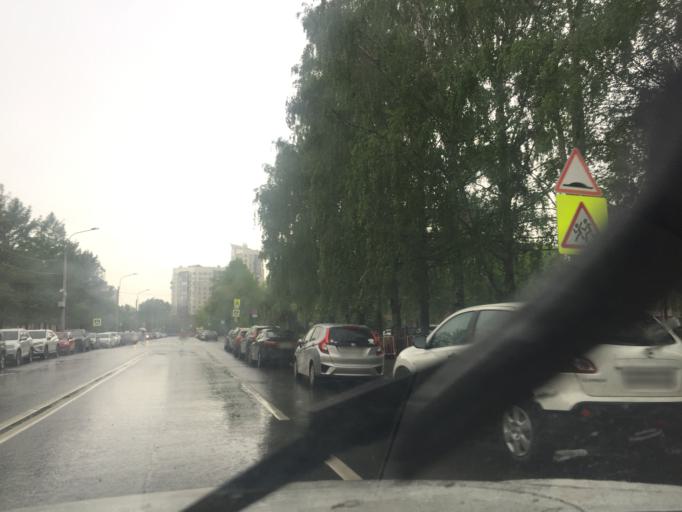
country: RU
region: St.-Petersburg
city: Vasyl'evsky Ostrov
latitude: 59.9321
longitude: 30.2525
